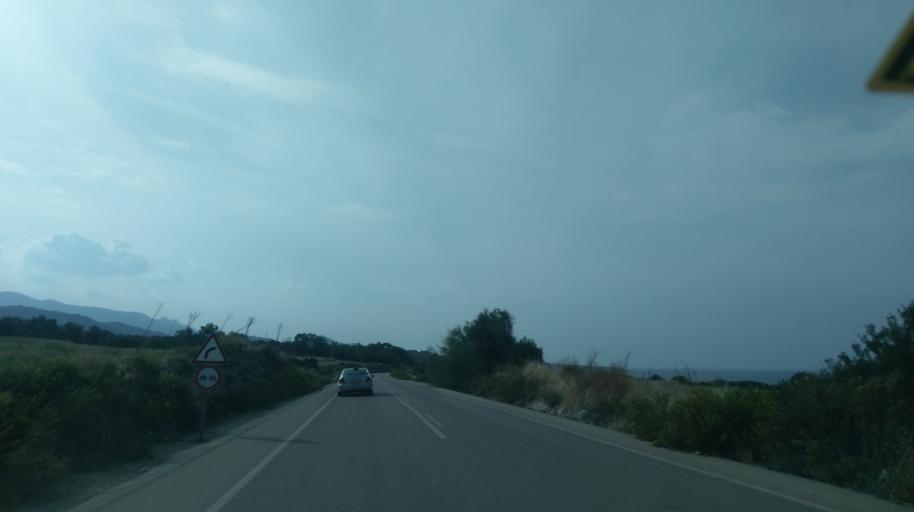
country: CY
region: Ammochostos
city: Trikomo
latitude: 35.4118
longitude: 33.8552
